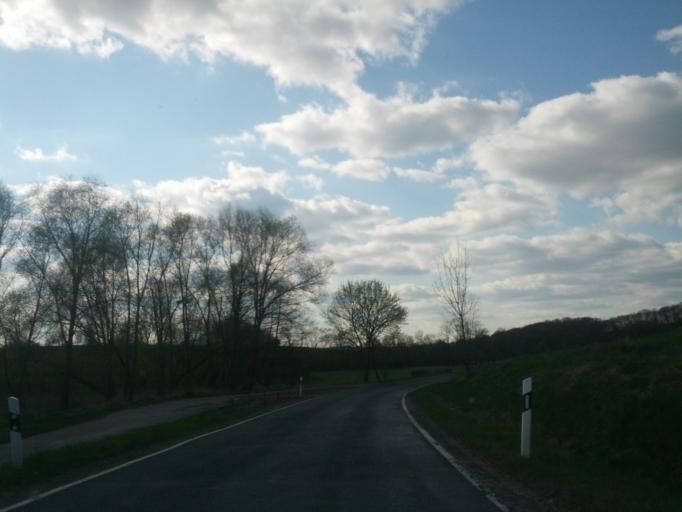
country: DE
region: Thuringia
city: Seebach
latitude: 50.9754
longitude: 10.4460
